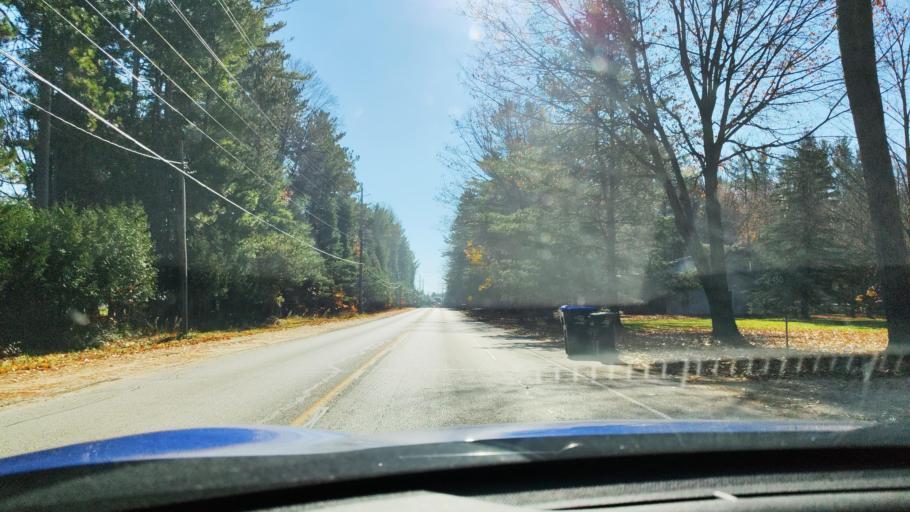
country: CA
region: Ontario
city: Wasaga Beach
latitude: 44.5156
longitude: -79.9951
